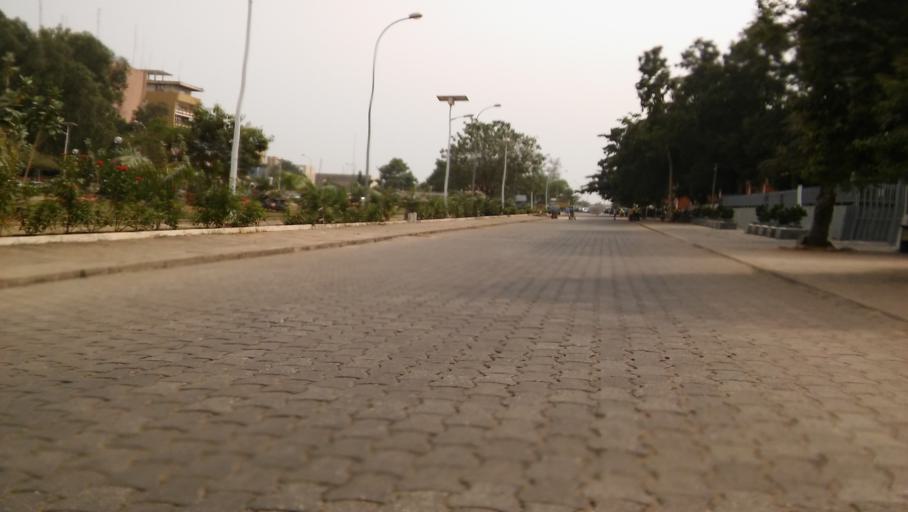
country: BJ
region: Littoral
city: Cotonou
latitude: 6.3552
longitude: 2.4072
